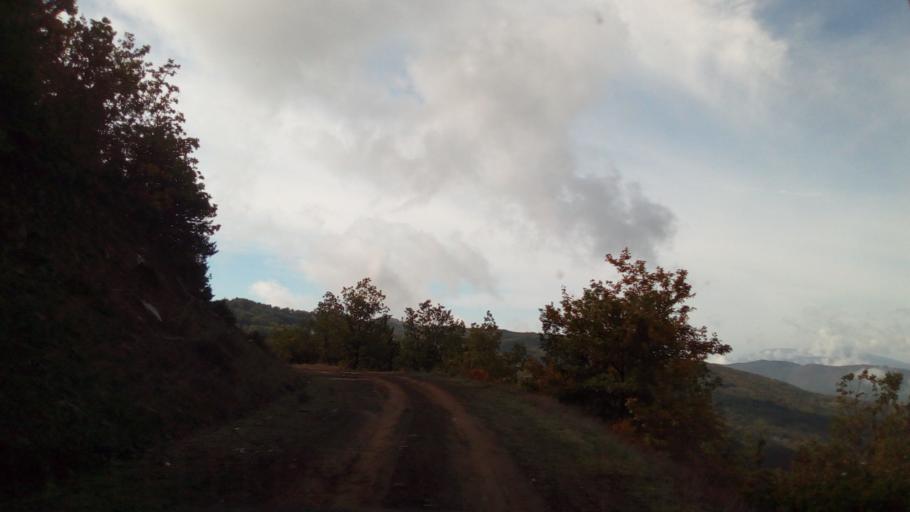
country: GR
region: Central Greece
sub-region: Nomos Fokidos
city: Lidoriki
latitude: 38.4795
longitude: 22.0507
